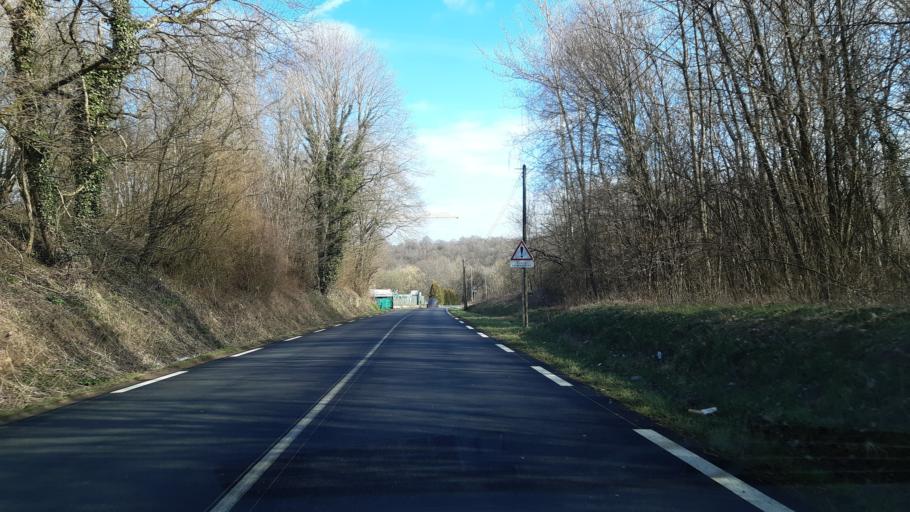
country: FR
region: Lorraine
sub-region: Departement de la Moselle
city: Audun-le-Tiche
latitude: 49.4601
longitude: 5.9634
